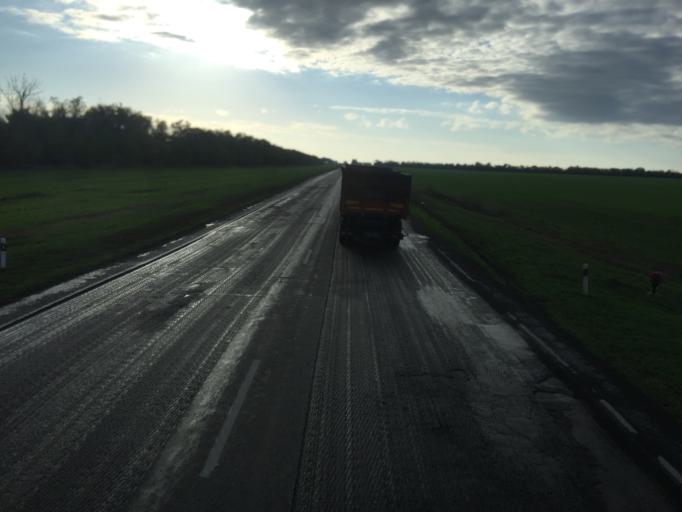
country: RU
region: Rostov
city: Kagal'nitskaya
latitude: 46.8567
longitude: 40.1929
